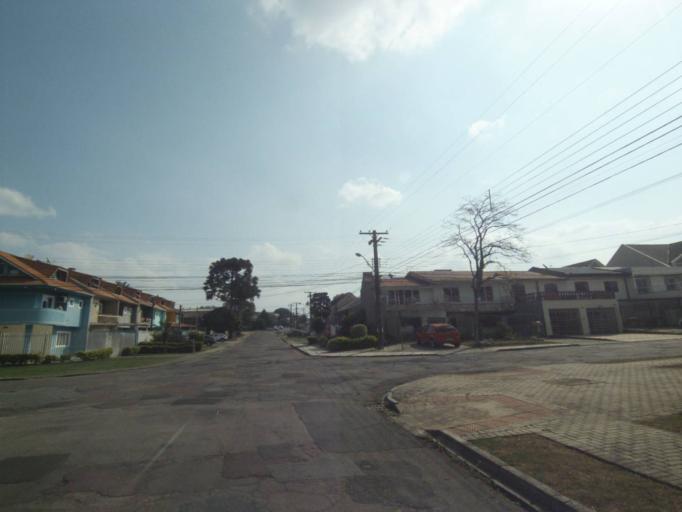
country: BR
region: Parana
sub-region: Sao Jose Dos Pinhais
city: Sao Jose dos Pinhais
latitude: -25.5122
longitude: -49.2432
